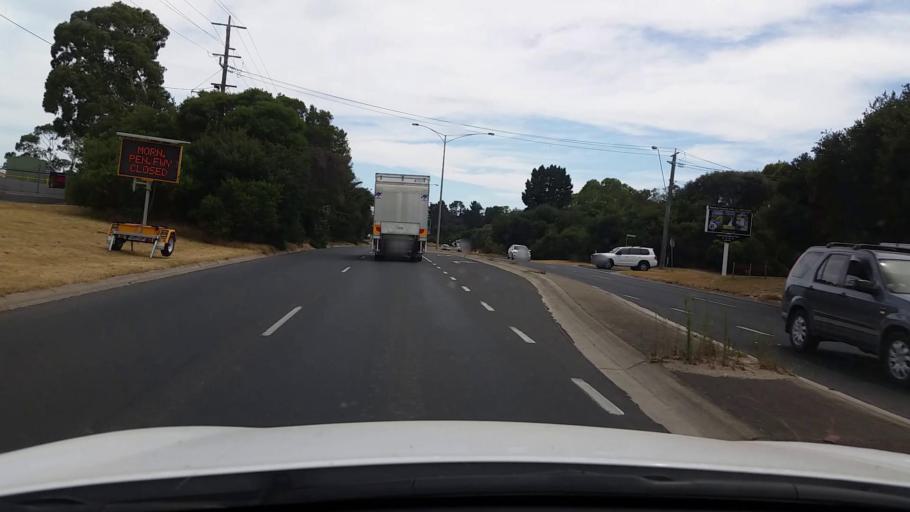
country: AU
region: Victoria
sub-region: Mornington Peninsula
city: Rosebud West
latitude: -38.3791
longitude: 144.8890
